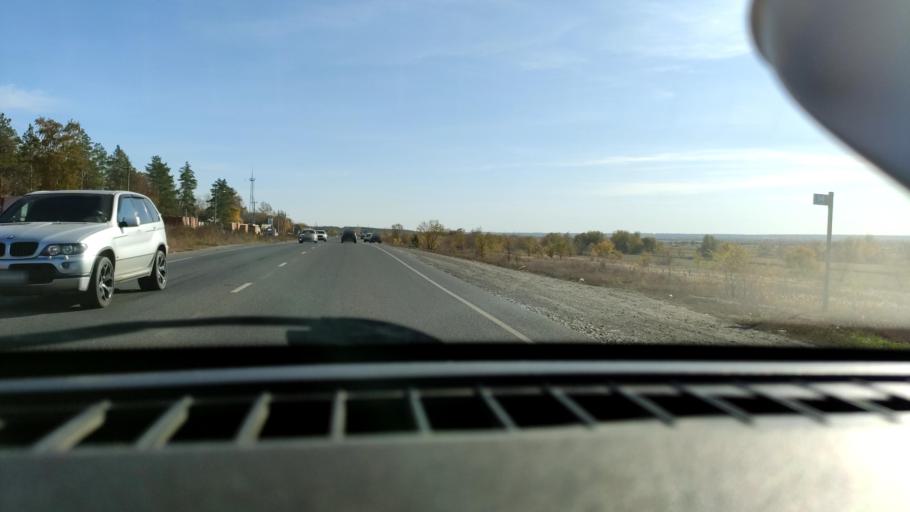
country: RU
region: Samara
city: Samara
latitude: 53.1251
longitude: 50.1797
